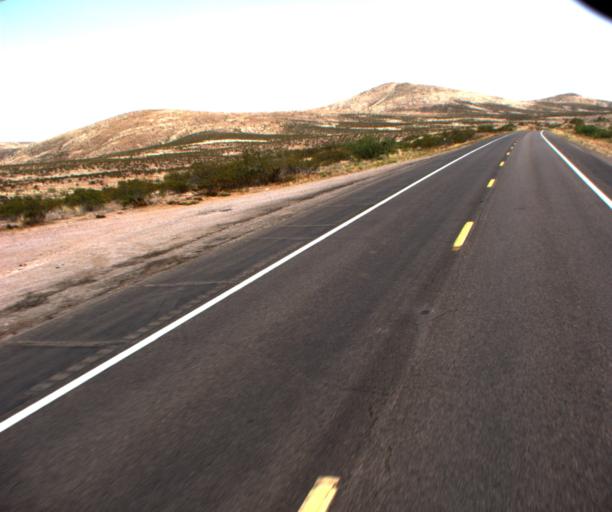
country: US
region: Arizona
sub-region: Greenlee County
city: Clifton
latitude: 32.7438
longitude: -109.2140
